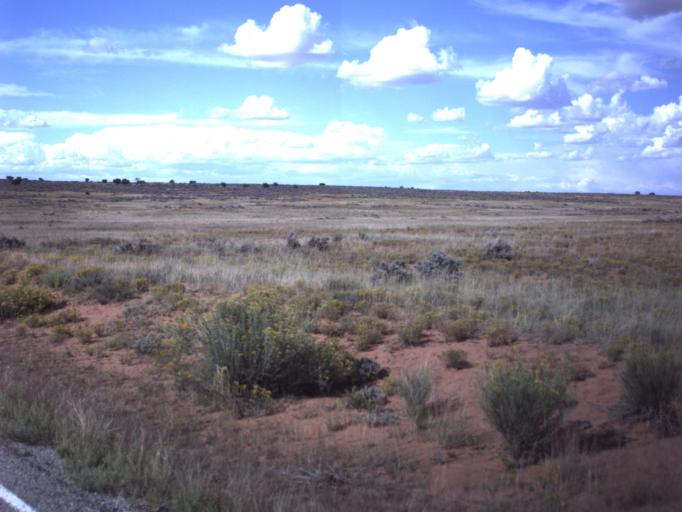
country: US
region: Utah
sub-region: Grand County
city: Moab
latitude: 38.5308
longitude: -109.7512
